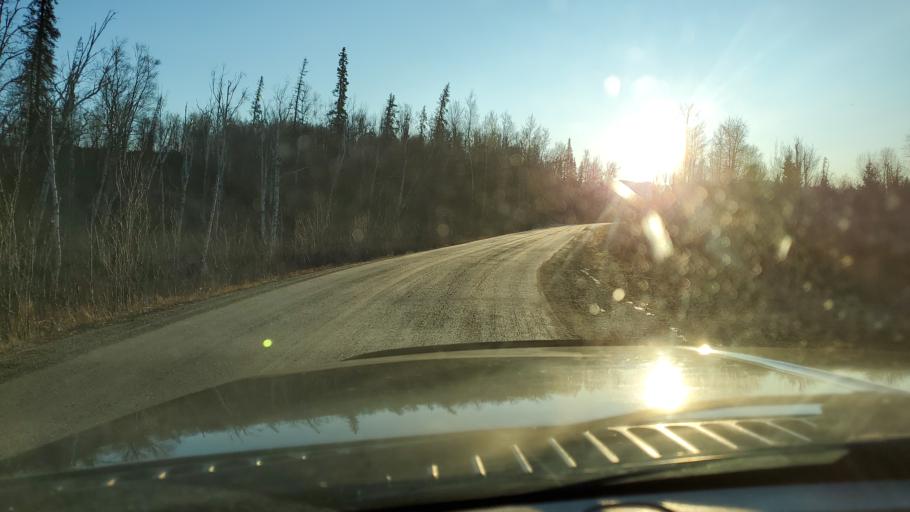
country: US
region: Alaska
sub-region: Matanuska-Susitna Borough
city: Gateway
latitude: 61.5896
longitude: -149.2696
